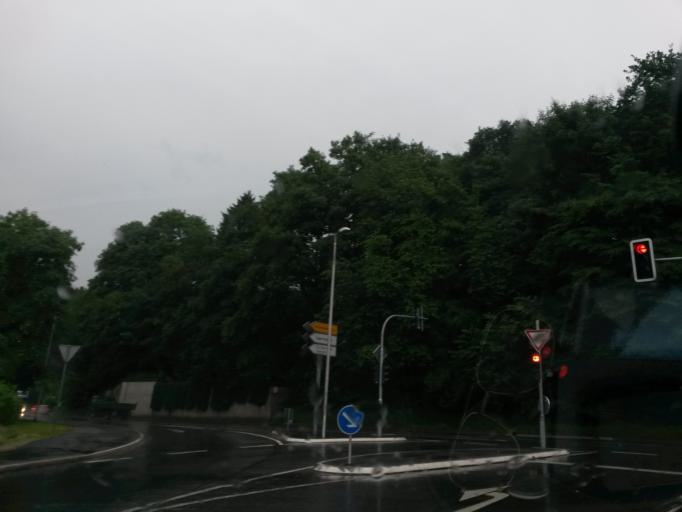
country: DE
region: North Rhine-Westphalia
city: Meinerzhagen
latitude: 51.1119
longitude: 7.6394
